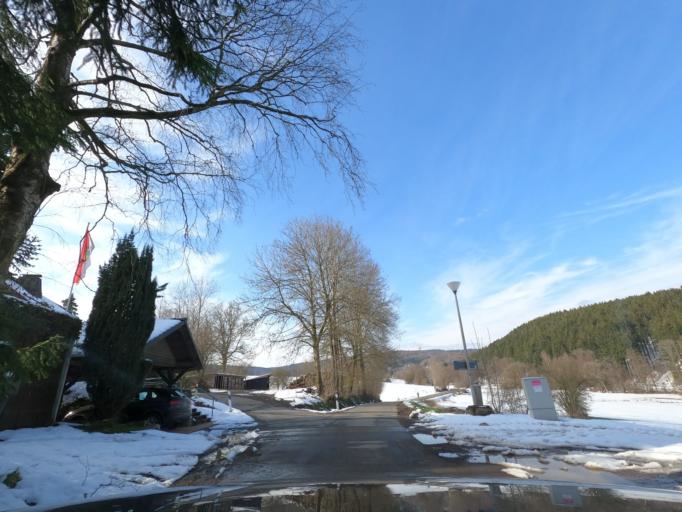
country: DE
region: North Rhine-Westphalia
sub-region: Regierungsbezirk Arnsberg
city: Herscheid
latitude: 51.1172
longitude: 7.7765
